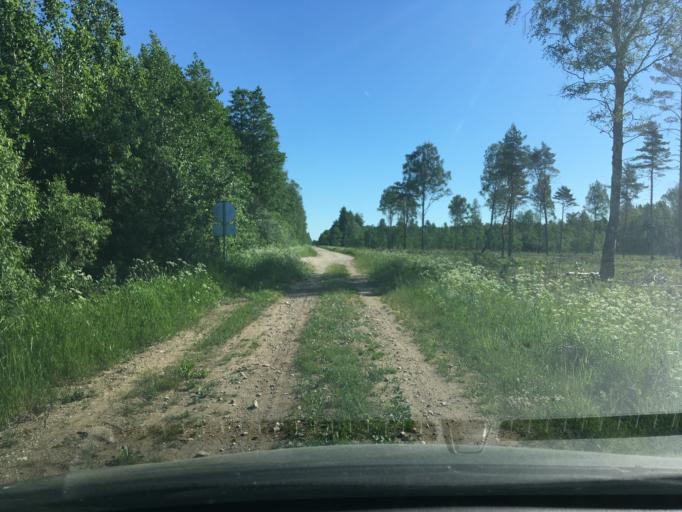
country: EE
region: Laeaene
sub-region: Lihula vald
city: Lihula
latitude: 58.6360
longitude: 23.7544
